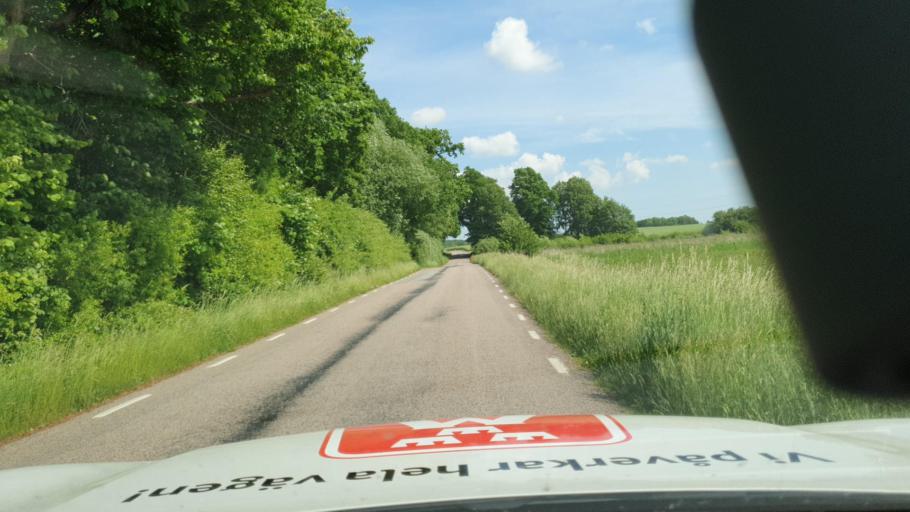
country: SE
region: Skane
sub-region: Svedala Kommun
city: Svedala
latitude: 55.5339
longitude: 13.1996
